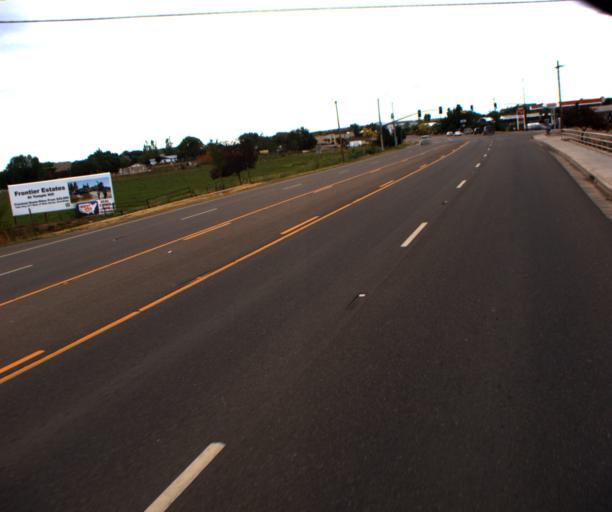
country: US
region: Arizona
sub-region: Navajo County
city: Taylor
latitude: 34.4705
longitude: -110.0901
